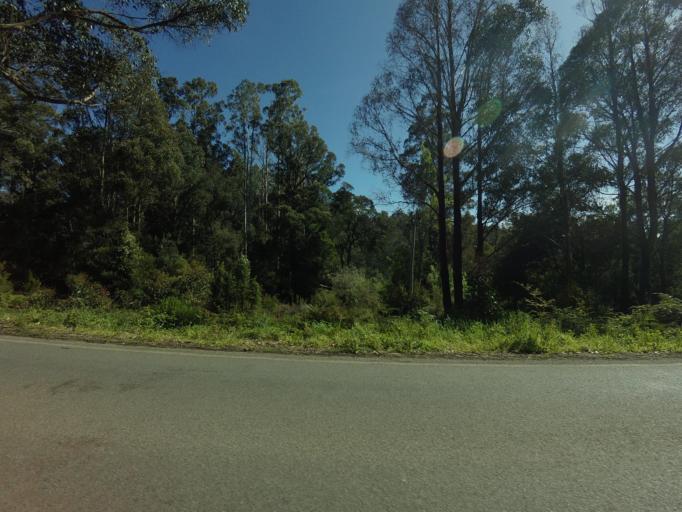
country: AU
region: Tasmania
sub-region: Derwent Valley
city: New Norfolk
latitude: -42.7129
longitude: 146.6984
